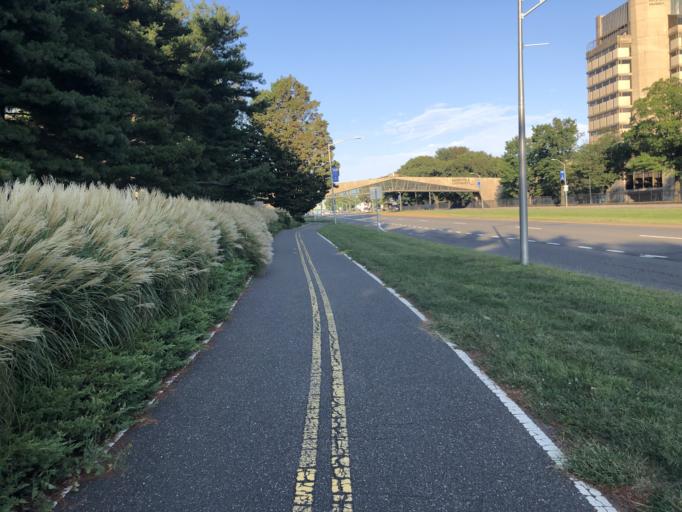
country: US
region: New York
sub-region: Nassau County
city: East Garden City
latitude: 40.7151
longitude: -73.6022
